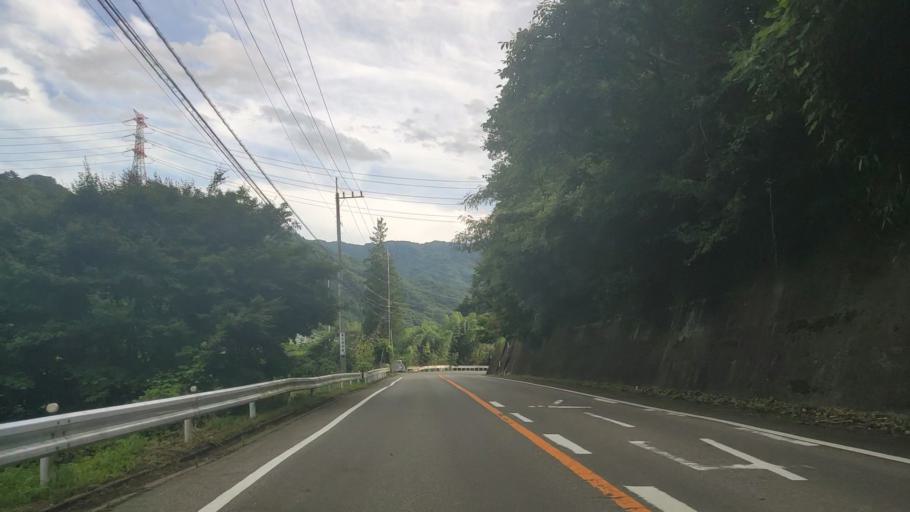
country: JP
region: Gunma
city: Kiryu
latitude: 36.5894
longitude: 139.4006
